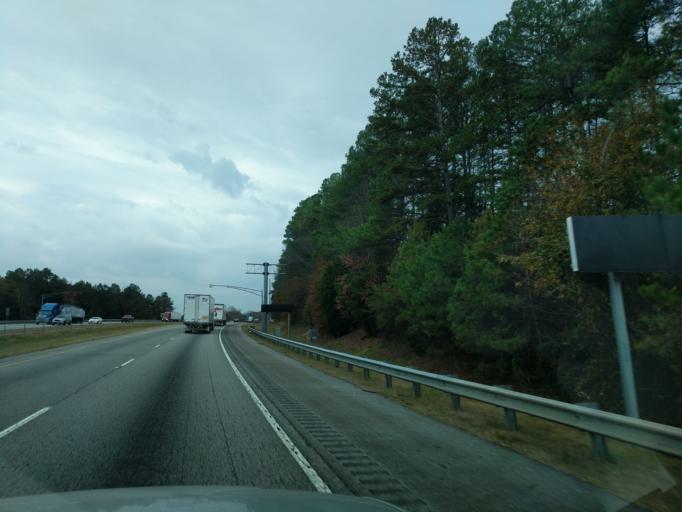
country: US
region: Georgia
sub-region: Franklin County
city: Lavonia
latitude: 34.4195
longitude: -83.1675
